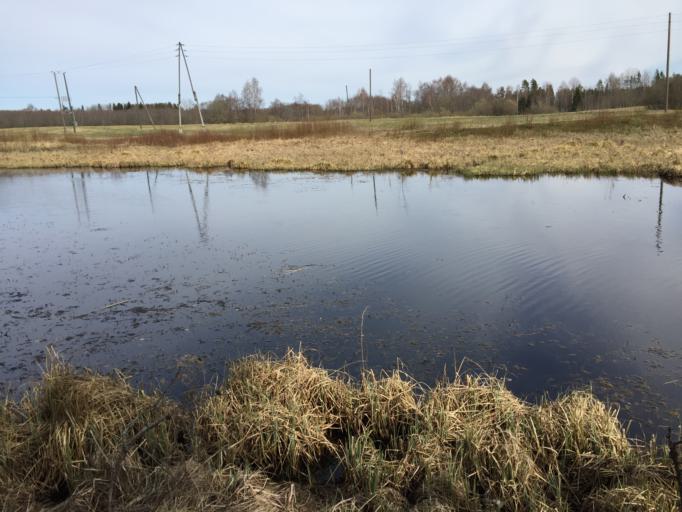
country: LV
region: Strenci
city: Seda
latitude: 57.8126
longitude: 25.8317
